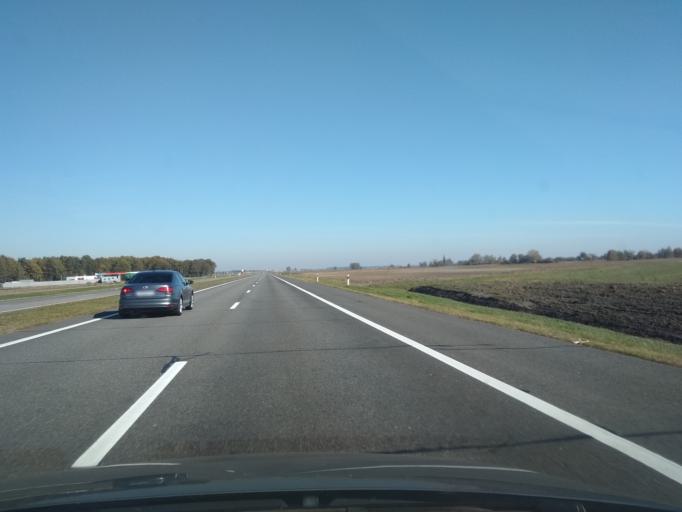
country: BY
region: Brest
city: Byaroza
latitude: 52.4123
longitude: 24.8108
